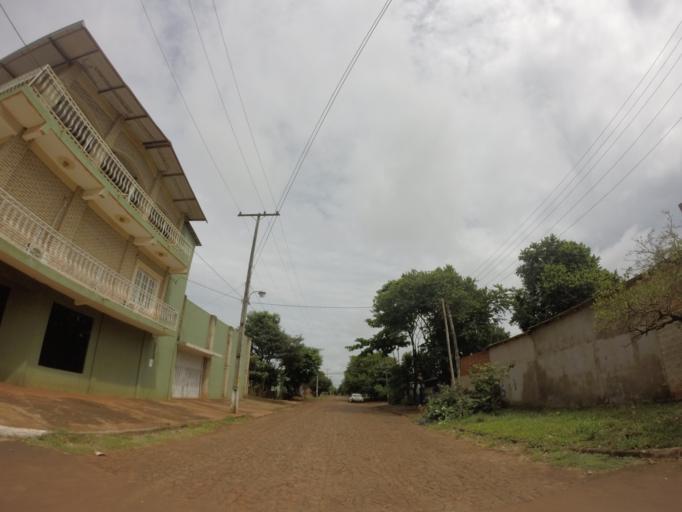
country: PY
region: Alto Parana
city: Ciudad del Este
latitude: -25.3843
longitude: -54.6543
